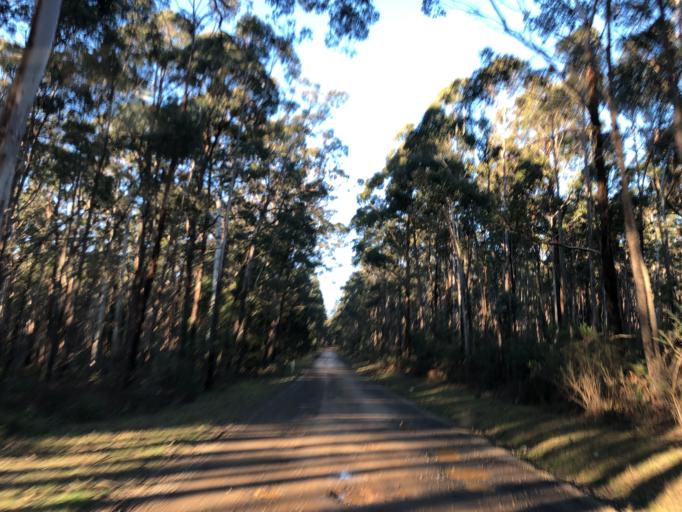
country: AU
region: Victoria
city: Brown Hill
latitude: -37.4783
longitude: 144.1617
